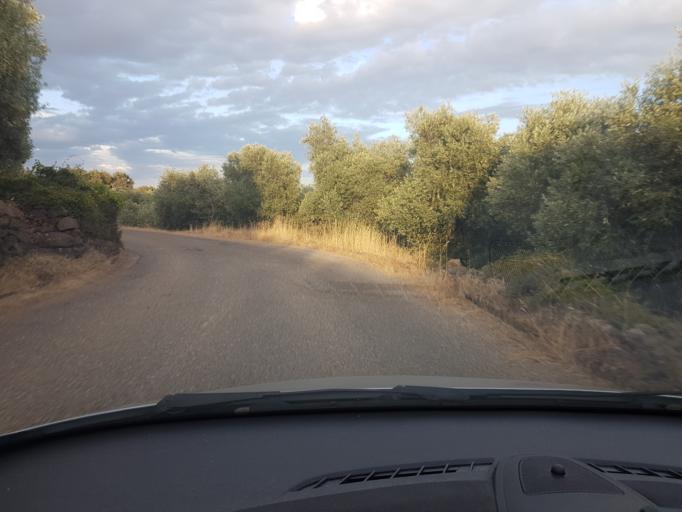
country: IT
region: Sardinia
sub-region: Provincia di Oristano
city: Seneghe
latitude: 40.0930
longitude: 8.6223
